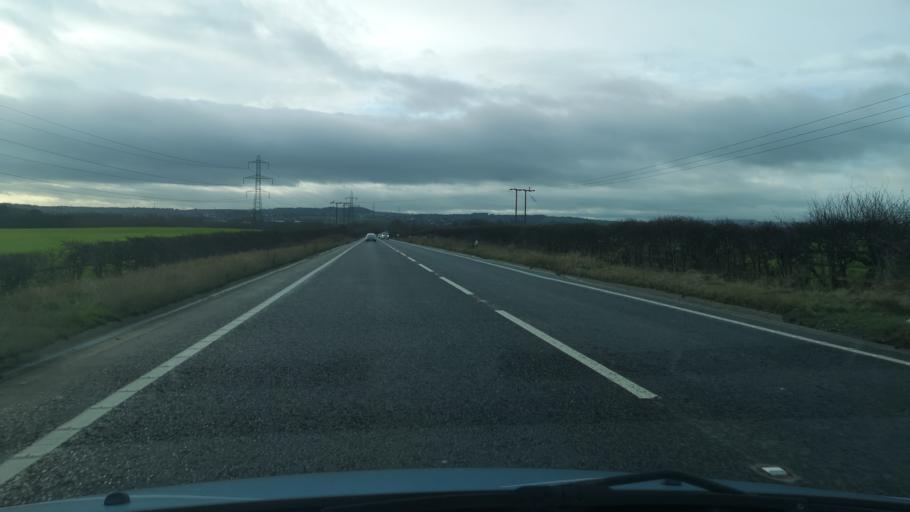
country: GB
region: England
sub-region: Barnsley
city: Little Houghton
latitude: 53.5297
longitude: -1.3568
